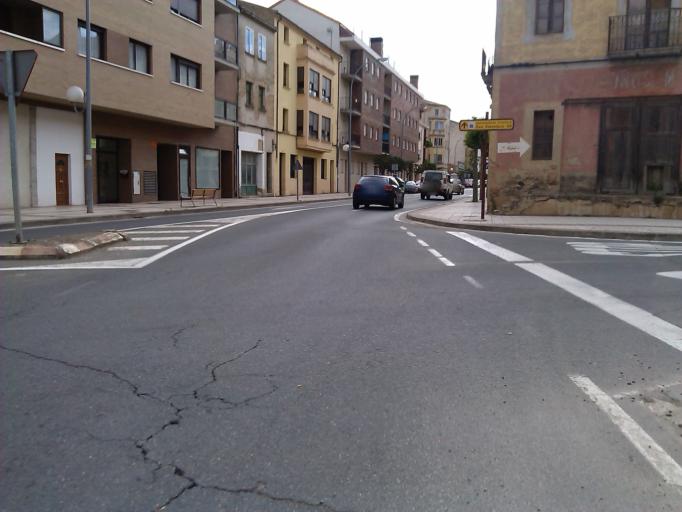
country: ES
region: La Rioja
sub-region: Provincia de La Rioja
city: Santo Domingo de la Calzada
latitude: 42.4394
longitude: -2.9451
